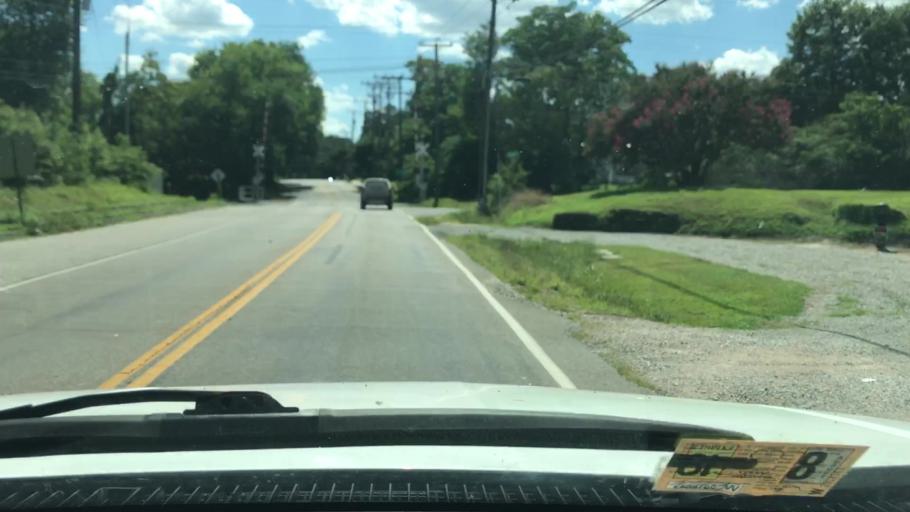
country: US
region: Virginia
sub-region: Henrico County
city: East Highland Park
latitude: 37.5730
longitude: -77.4099
